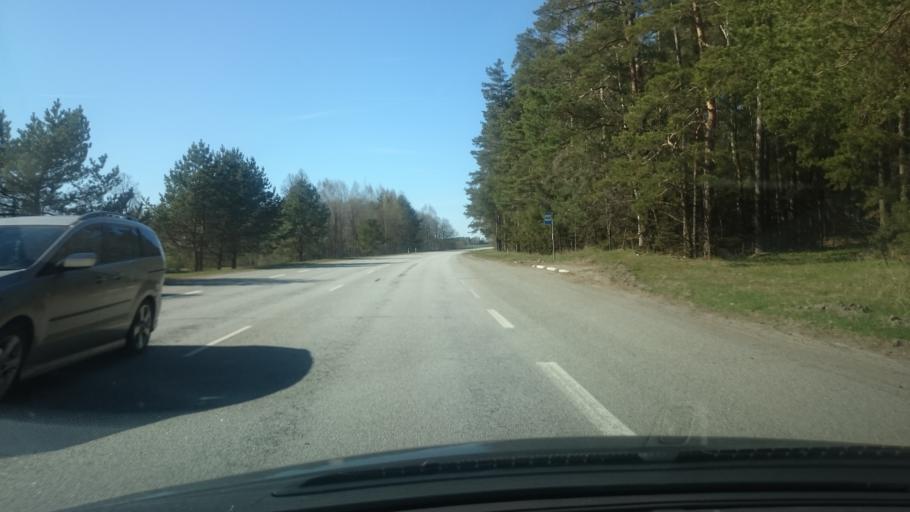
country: EE
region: Tartu
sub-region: UElenurme vald
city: Ulenurme
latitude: 58.3146
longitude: 26.9893
